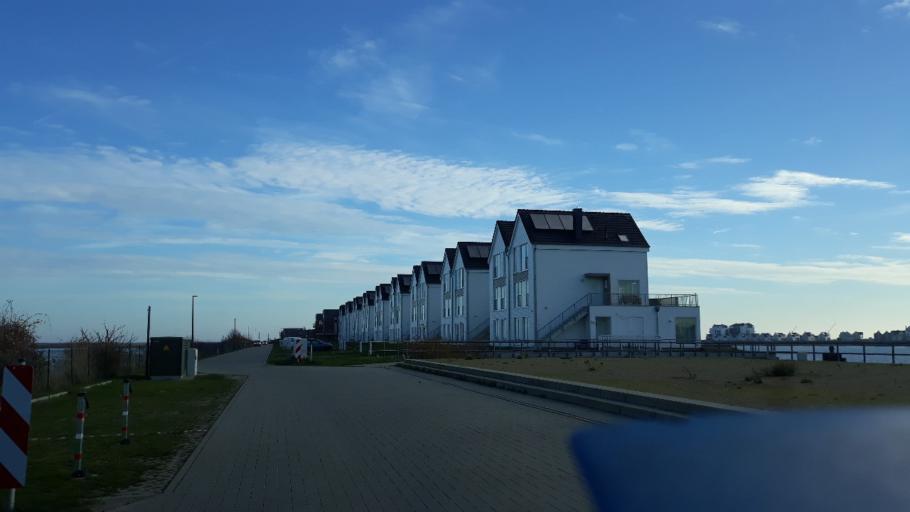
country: DE
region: Schleswig-Holstein
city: Maasholm
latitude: 54.6638
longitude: 10.0213
